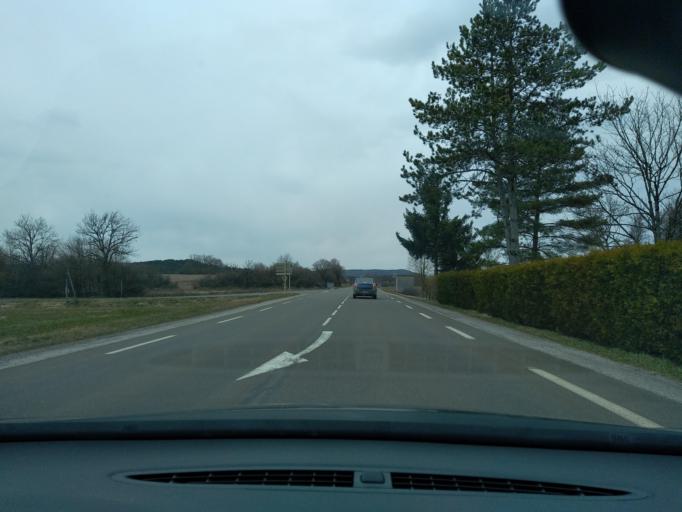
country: FR
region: Franche-Comte
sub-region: Departement du Jura
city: Arinthod
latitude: 46.4213
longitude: 5.5548
